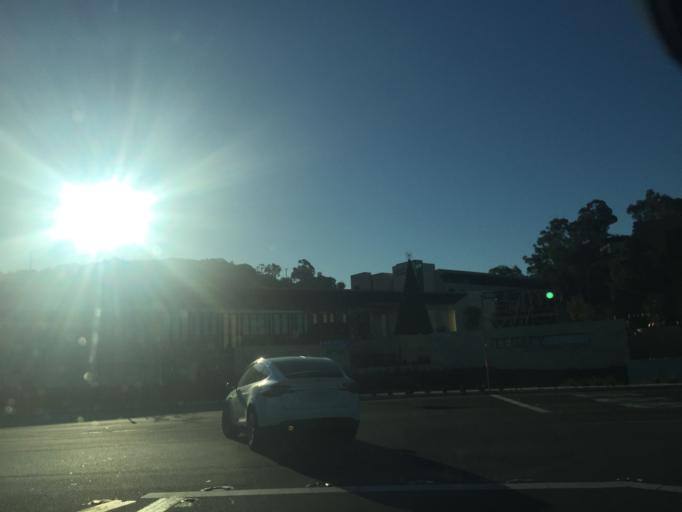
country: US
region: California
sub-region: San Diego County
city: San Diego
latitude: 32.7599
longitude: -117.1710
